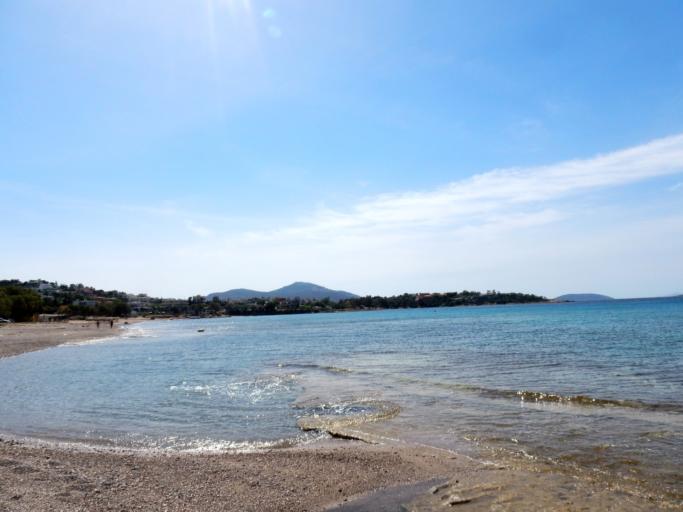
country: GR
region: Attica
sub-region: Nomarchia Anatolikis Attikis
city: Agios Dimitrios Kropias
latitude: 37.8014
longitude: 23.8662
